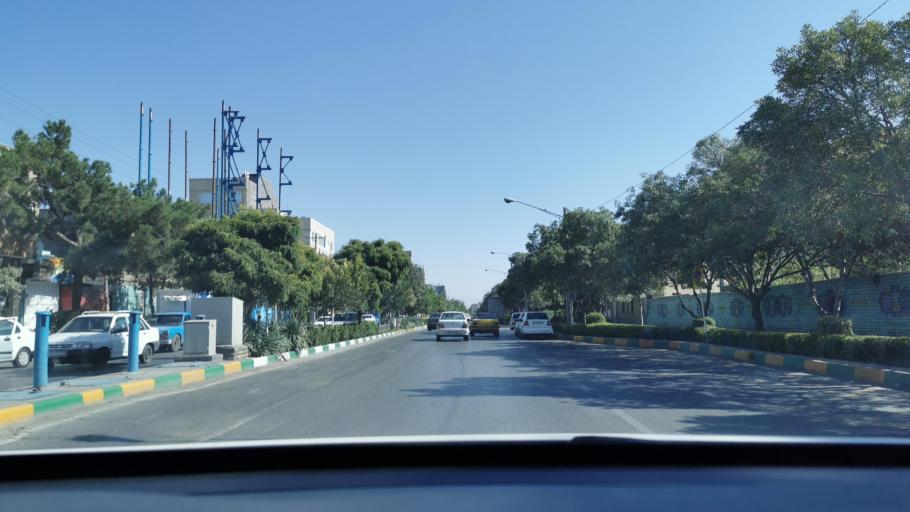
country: IR
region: Razavi Khorasan
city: Mashhad
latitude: 36.3314
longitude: 59.5907
